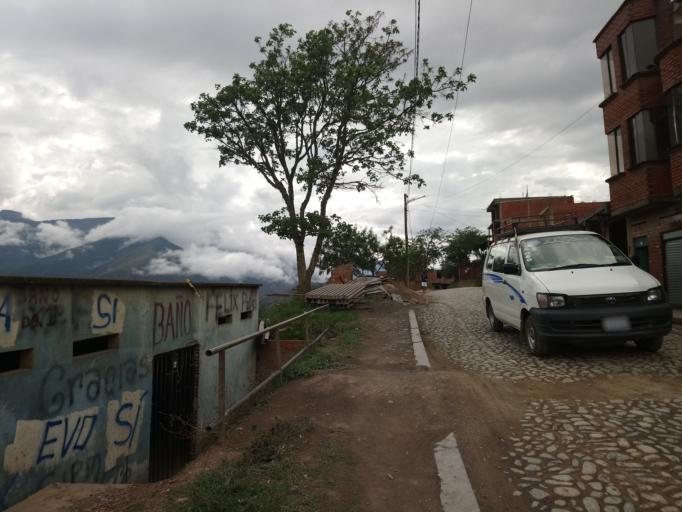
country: BO
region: La Paz
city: Coripata
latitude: -16.2700
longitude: -67.6399
